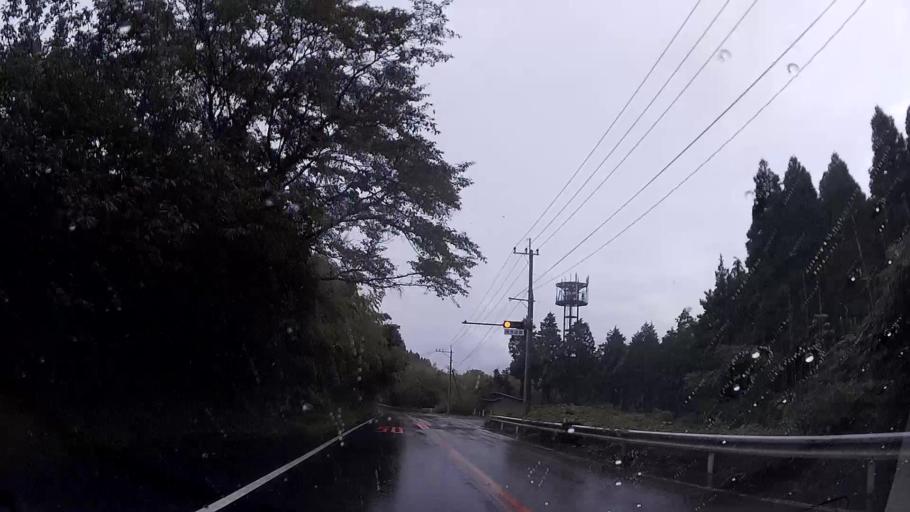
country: JP
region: Kumamoto
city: Aso
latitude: 32.8722
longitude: 130.9935
